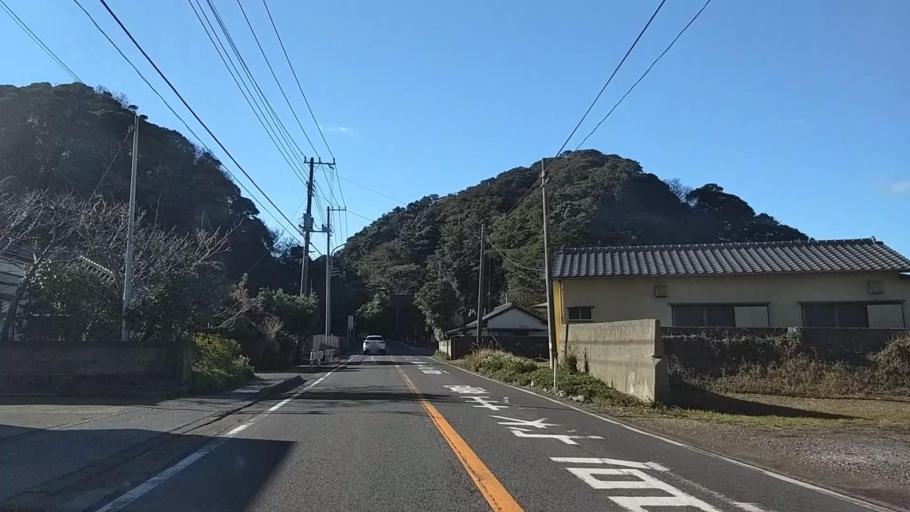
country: JP
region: Chiba
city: Futtsu
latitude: 35.1729
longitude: 139.8190
